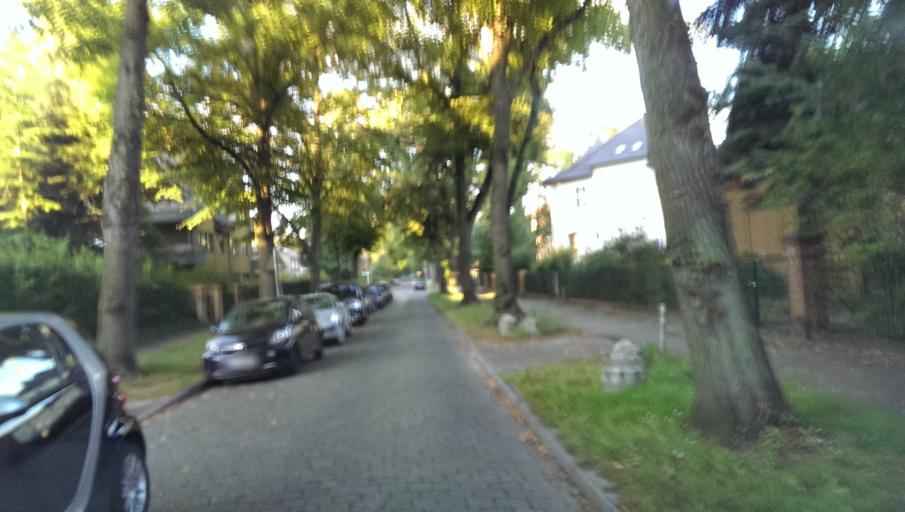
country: DE
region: Berlin
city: Lichterfelde
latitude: 52.4231
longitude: 13.3233
